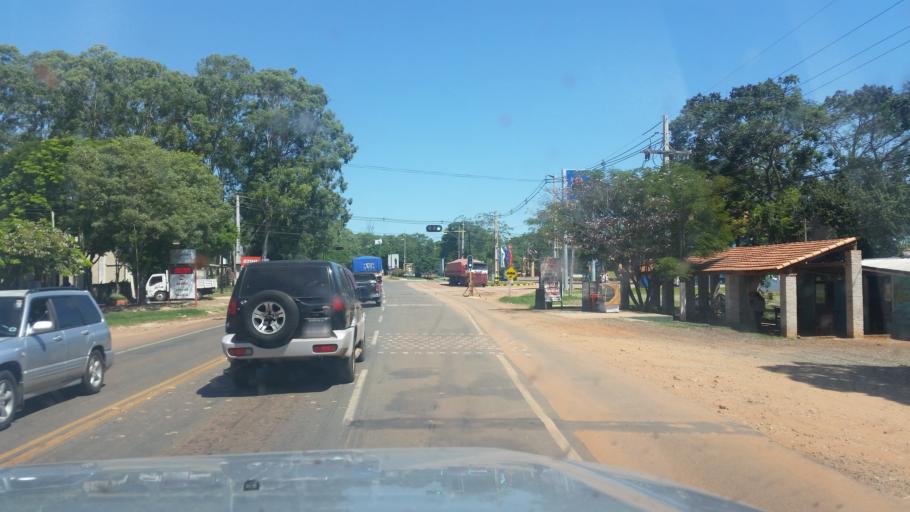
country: PY
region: Misiones
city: San Juan Bautista
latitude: -26.6658
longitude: -57.1329
